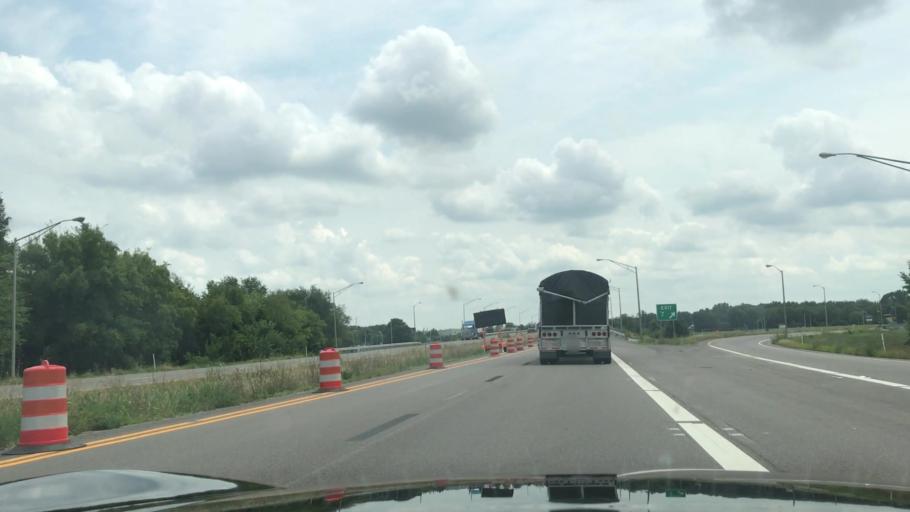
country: US
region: Kentucky
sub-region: Warren County
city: Bowling Green
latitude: 36.9610
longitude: -86.4979
